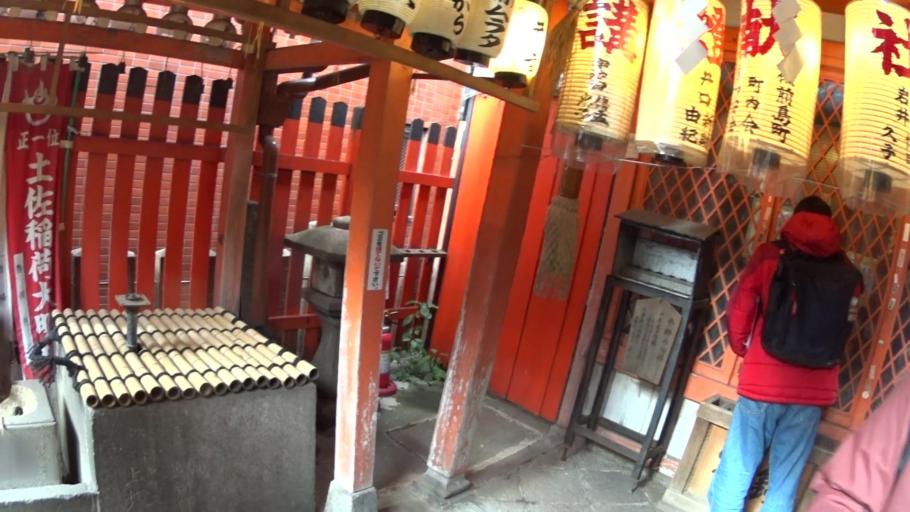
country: JP
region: Kyoto
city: Kyoto
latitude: 35.0063
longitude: 135.7688
